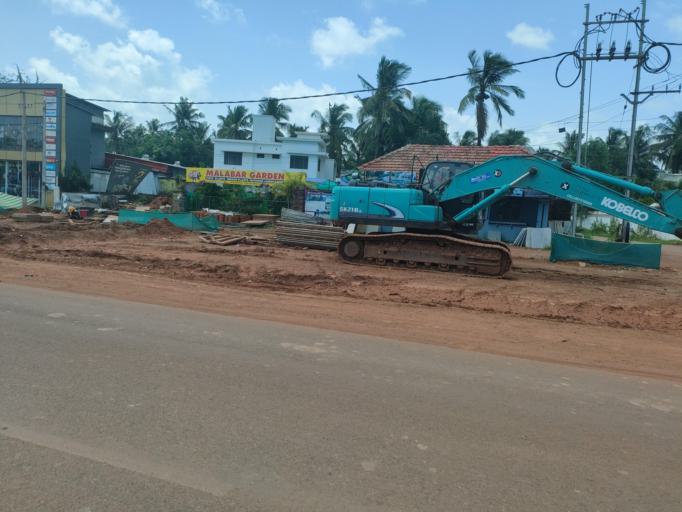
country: IN
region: Kerala
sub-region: Kasaragod District
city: Kasaragod
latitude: 12.5139
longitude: 75.0257
